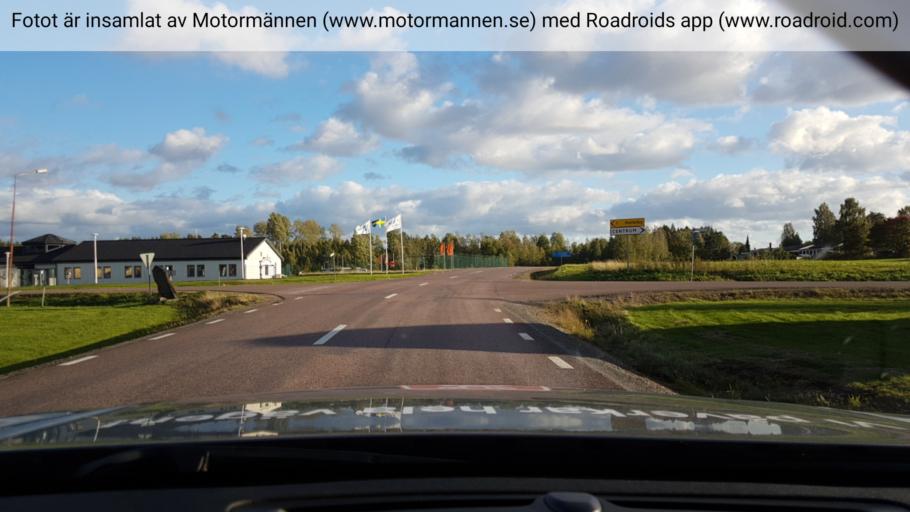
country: SE
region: Vaermland
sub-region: Karlstads Kommun
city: Molkom
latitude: 59.6067
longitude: 13.7383
